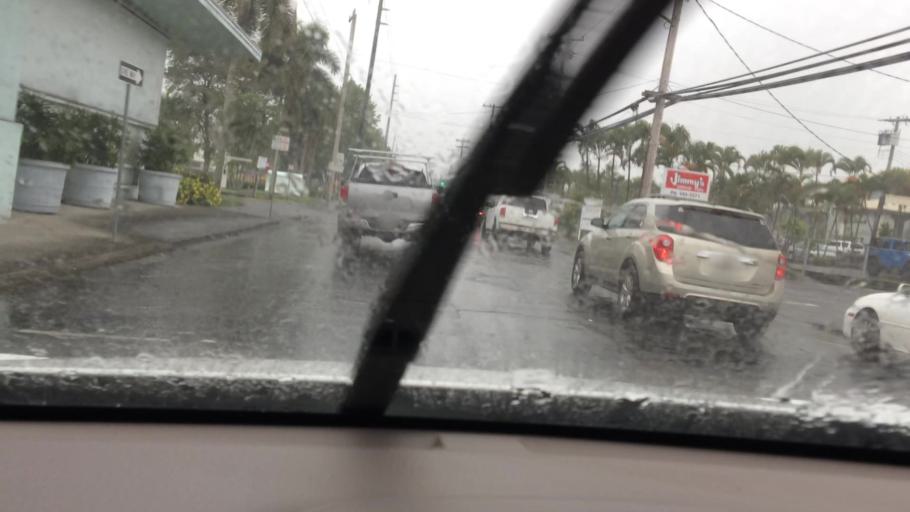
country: US
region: Hawaii
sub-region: Hawaii County
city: Hilo
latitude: 19.7219
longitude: -155.0870
